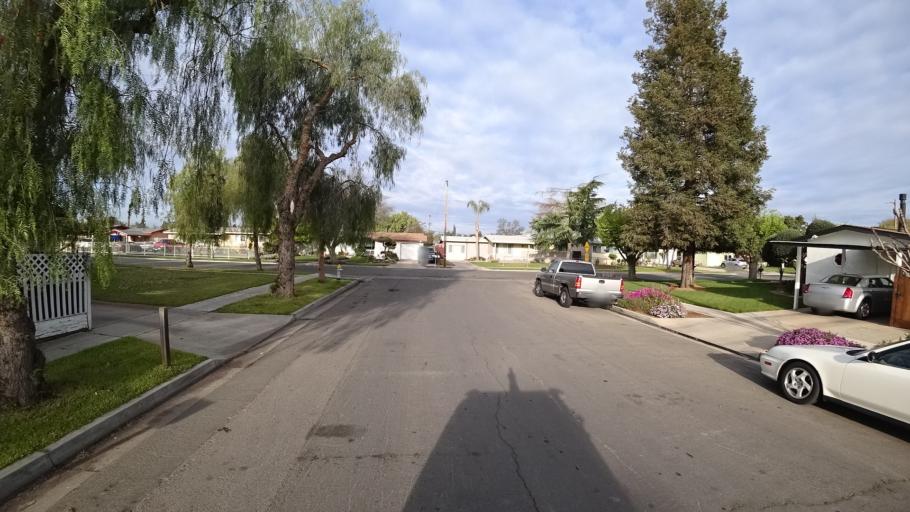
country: US
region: California
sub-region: Fresno County
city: Fresno
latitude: 36.8283
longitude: -119.7922
